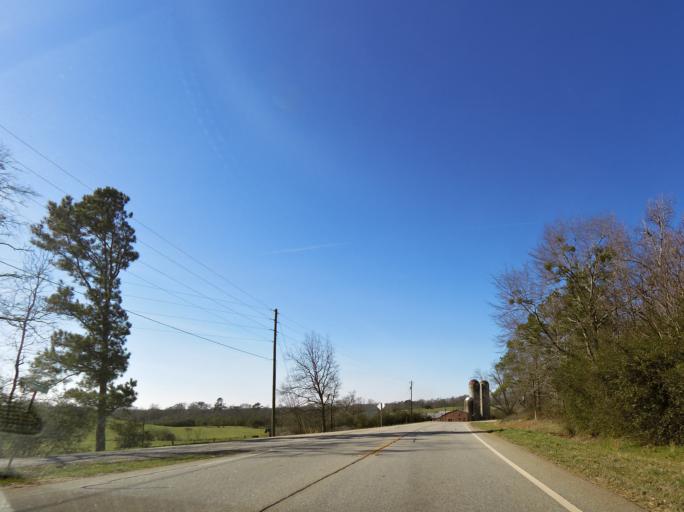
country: US
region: Georgia
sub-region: Crawford County
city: Roberta
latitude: 32.8809
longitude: -84.0945
